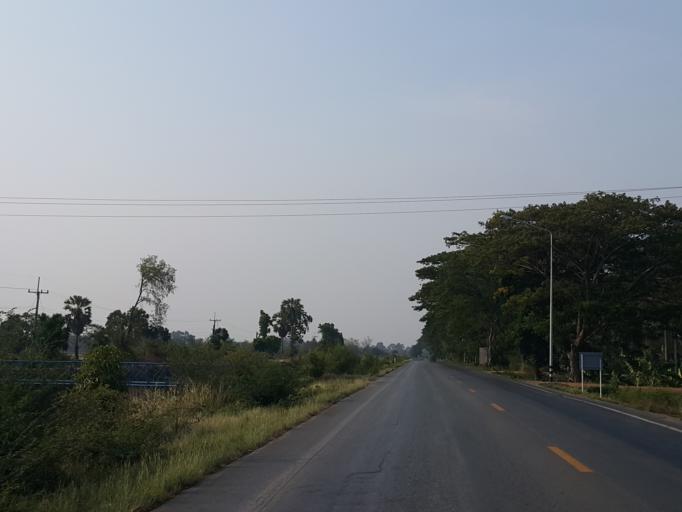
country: TH
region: Chai Nat
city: Sankhaburi
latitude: 15.0253
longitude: 100.1447
